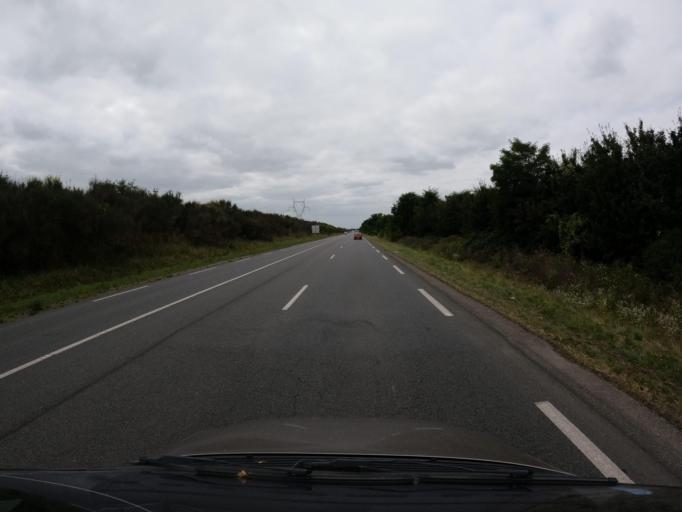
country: FR
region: Poitou-Charentes
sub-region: Departement des Deux-Sevres
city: Mougon
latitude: 46.2987
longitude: -0.3096
